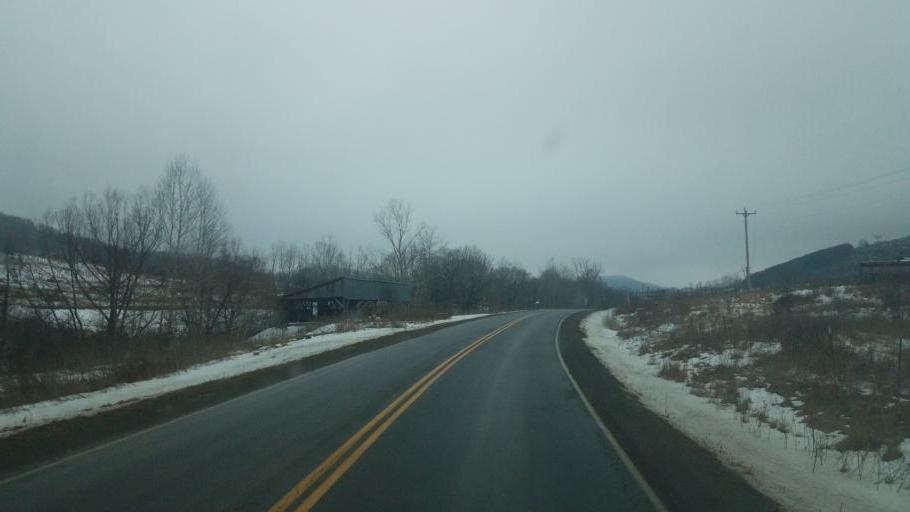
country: US
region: Pennsylvania
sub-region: Tioga County
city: Westfield
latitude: 42.0250
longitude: -77.5450
